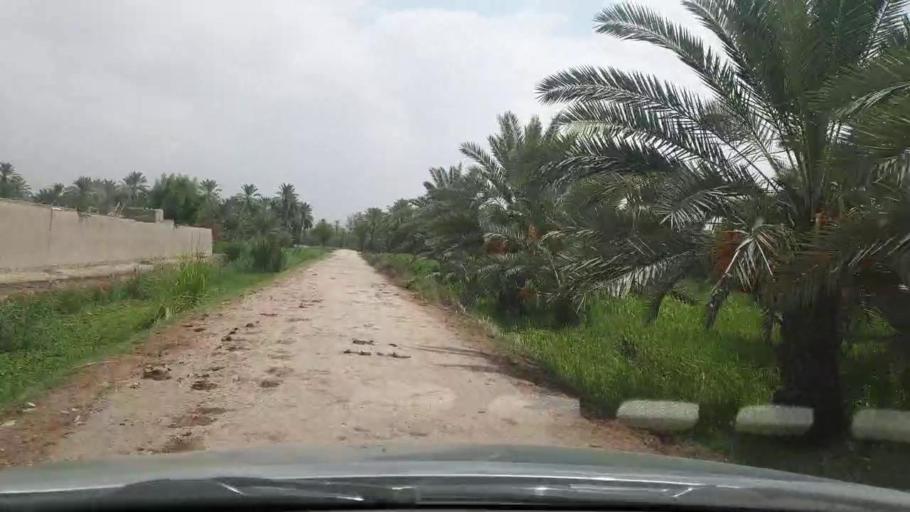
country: PK
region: Sindh
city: Kot Diji
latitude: 27.4111
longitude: 68.7614
